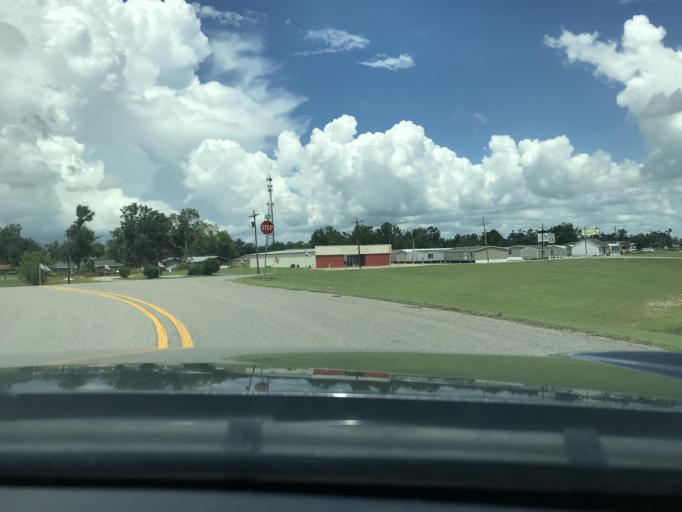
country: US
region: Louisiana
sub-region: Calcasieu Parish
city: Moss Bluff
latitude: 30.3092
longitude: -93.1944
